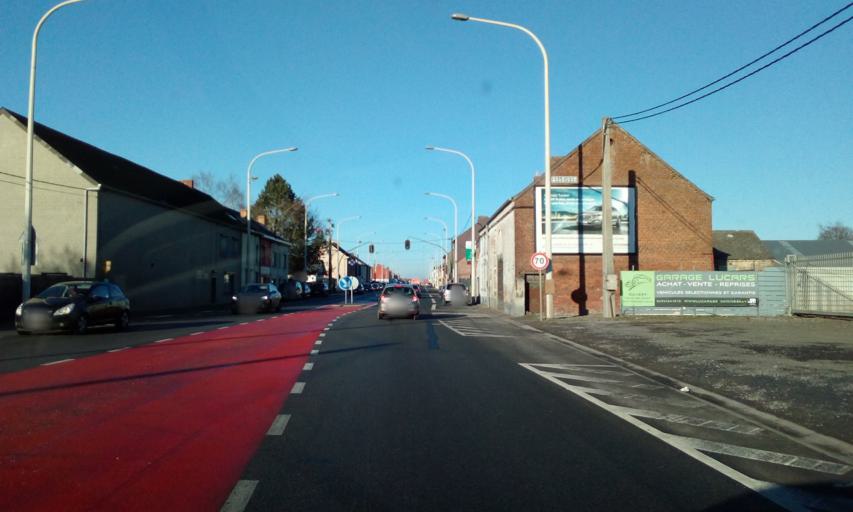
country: BE
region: Wallonia
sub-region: Province du Hainaut
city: Gerpinnes
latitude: 50.3367
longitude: 4.4747
